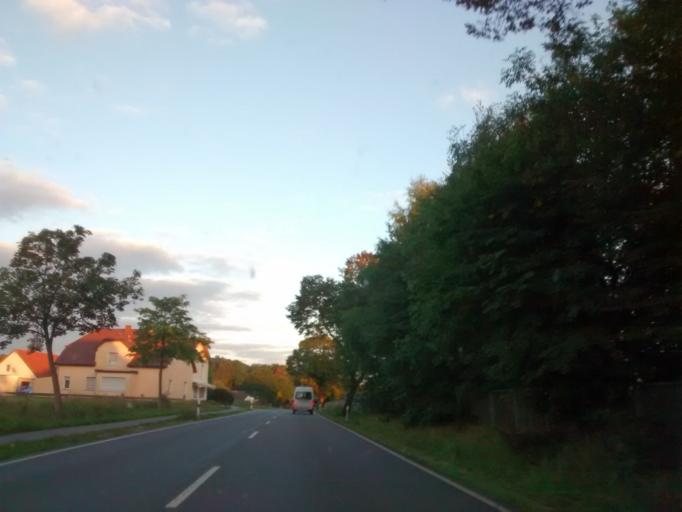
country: DE
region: North Rhine-Westphalia
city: Borgholzhausen
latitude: 52.0850
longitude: 8.2728
